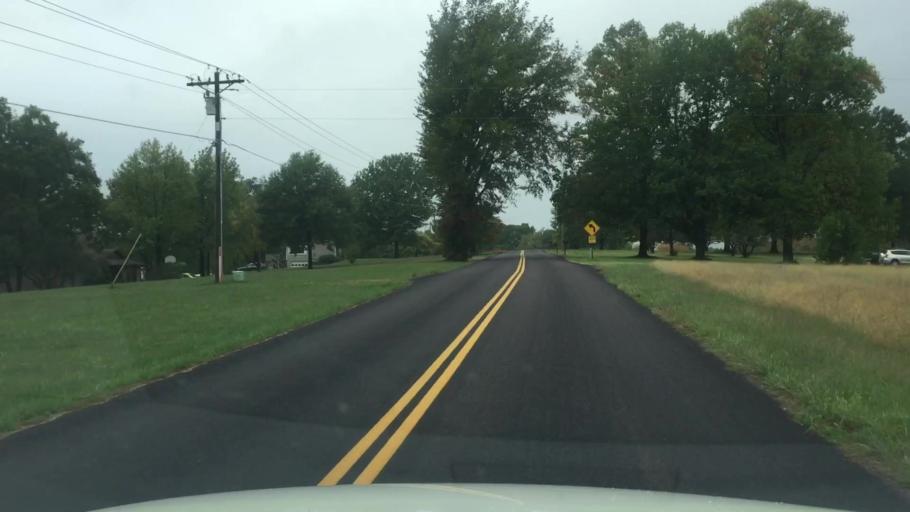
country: US
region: Missouri
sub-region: Boone County
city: Columbia
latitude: 38.8615
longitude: -92.3398
